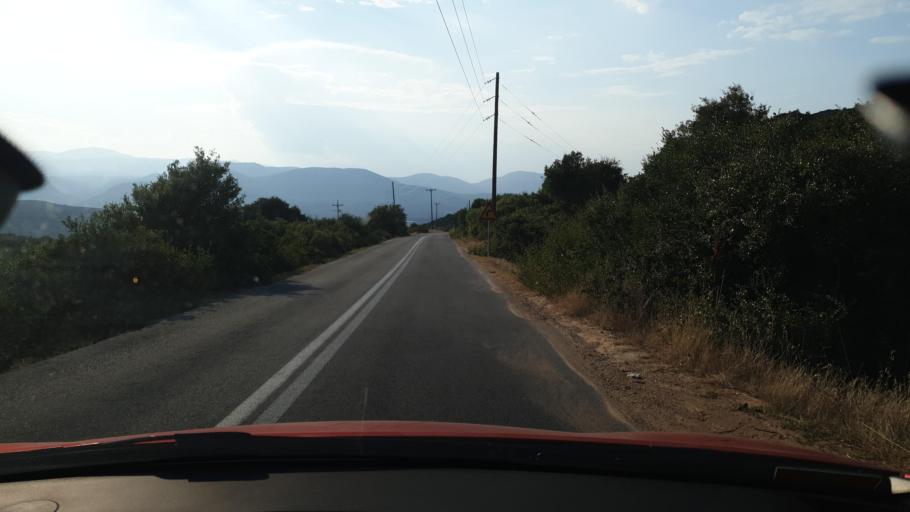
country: GR
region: Thessaly
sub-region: Nomos Magnisias
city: Pteleos
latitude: 39.0595
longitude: 22.9343
